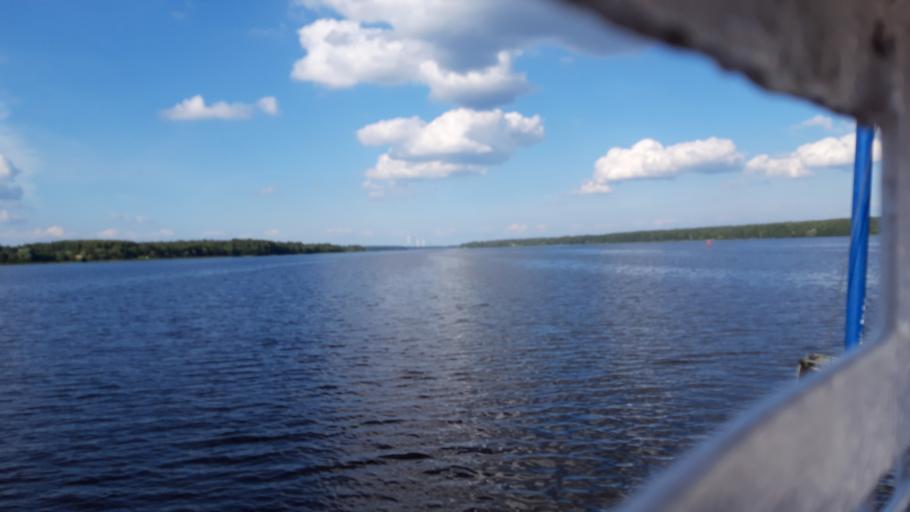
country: RU
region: Tverskaya
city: Konakovo
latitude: 56.6665
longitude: 36.6575
